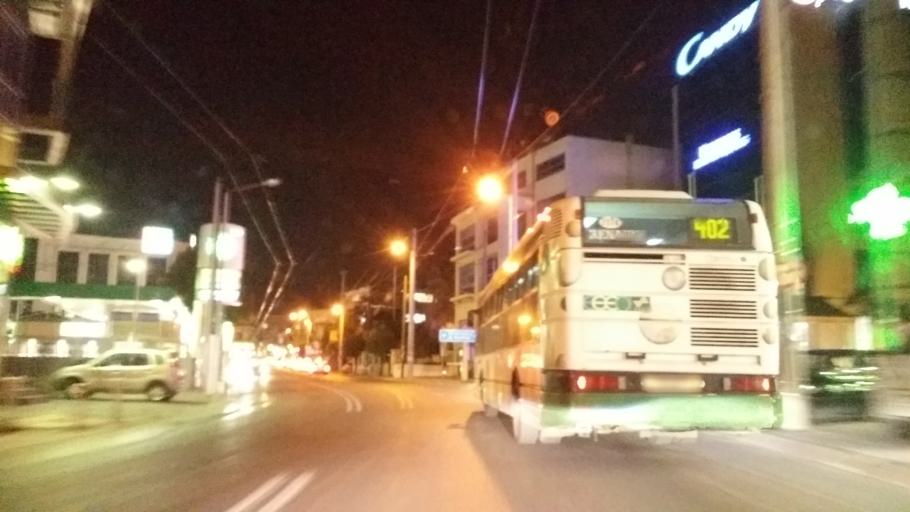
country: GR
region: Attica
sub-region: Nomarchia Athinas
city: Khalandrion
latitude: 38.0169
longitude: 23.7944
